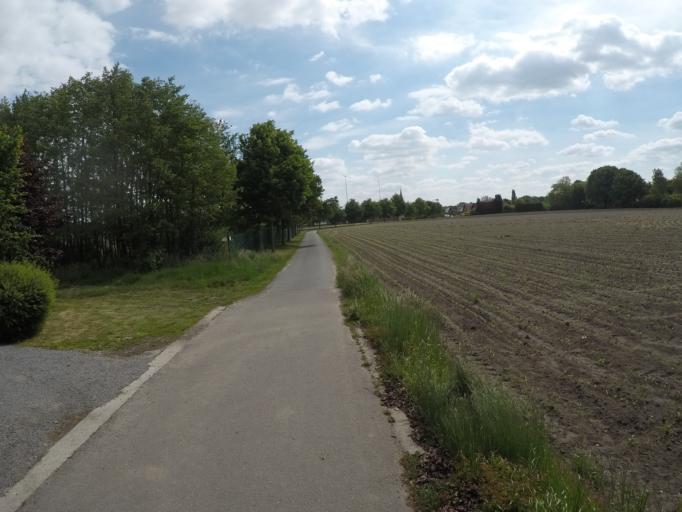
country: BE
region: Flanders
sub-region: Provincie Antwerpen
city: Zoersel
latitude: 51.3019
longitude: 4.6830
